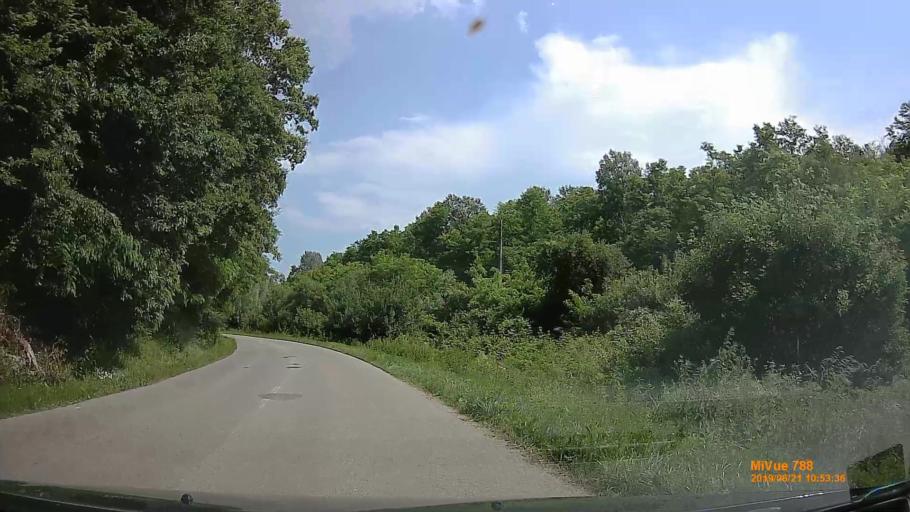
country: HU
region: Baranya
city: Buekkoesd
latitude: 46.1451
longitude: 18.0628
